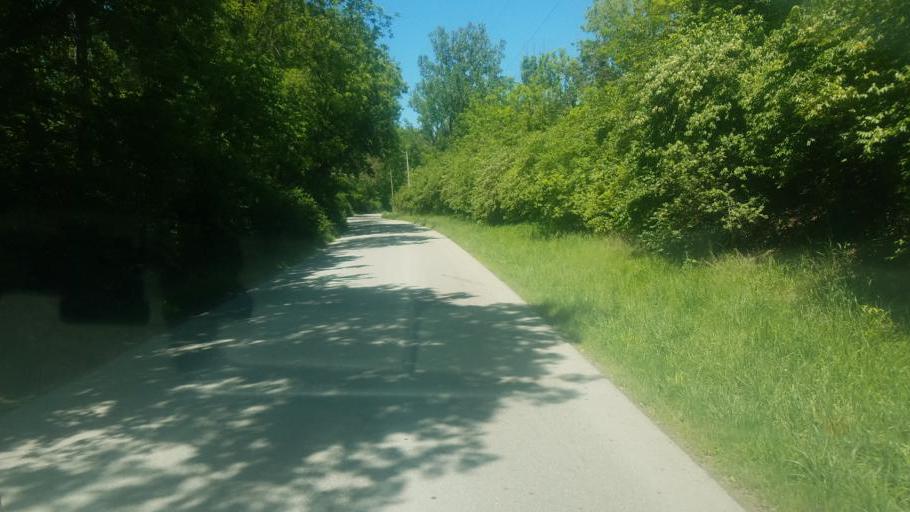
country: US
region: Ohio
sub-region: Miami County
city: Piqua
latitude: 40.2156
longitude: -84.2128
